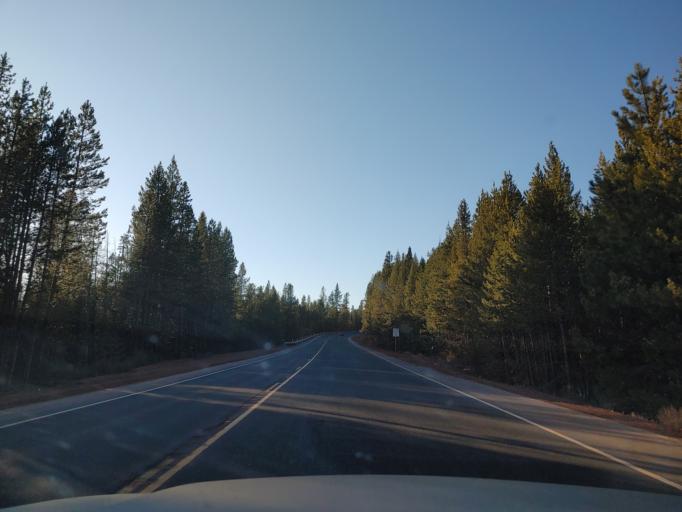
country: US
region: Oregon
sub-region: Deschutes County
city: La Pine
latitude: 43.4419
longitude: -121.8669
